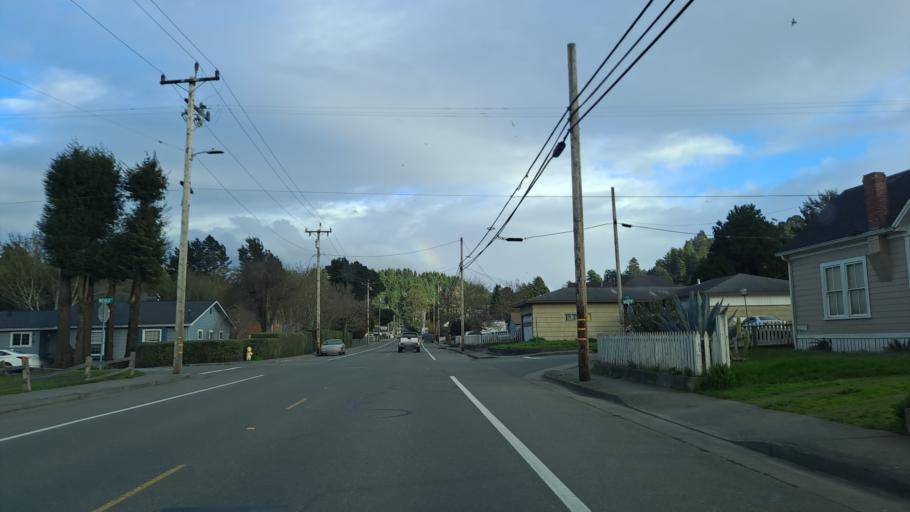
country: US
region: California
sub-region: Humboldt County
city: Fortuna
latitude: 40.5702
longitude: -124.1311
